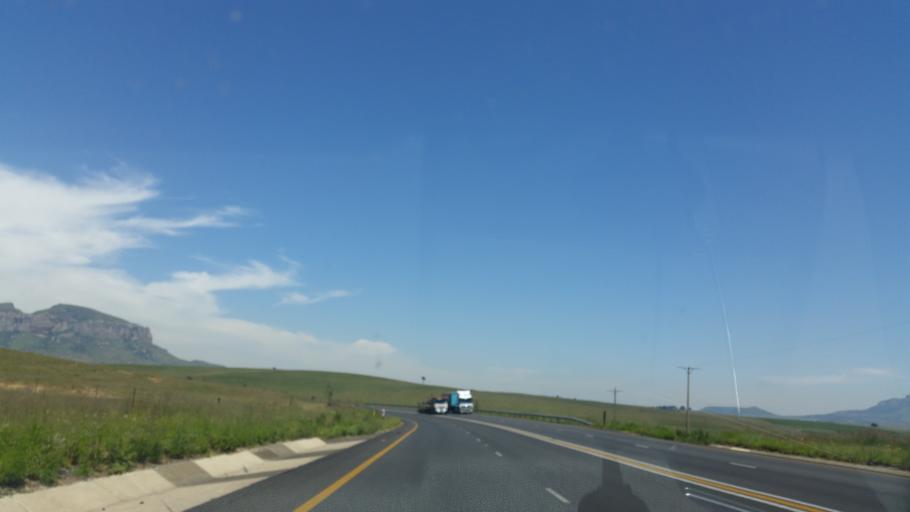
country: ZA
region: Orange Free State
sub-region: Thabo Mofutsanyana District Municipality
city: Harrismith
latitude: -28.3665
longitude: 29.3430
